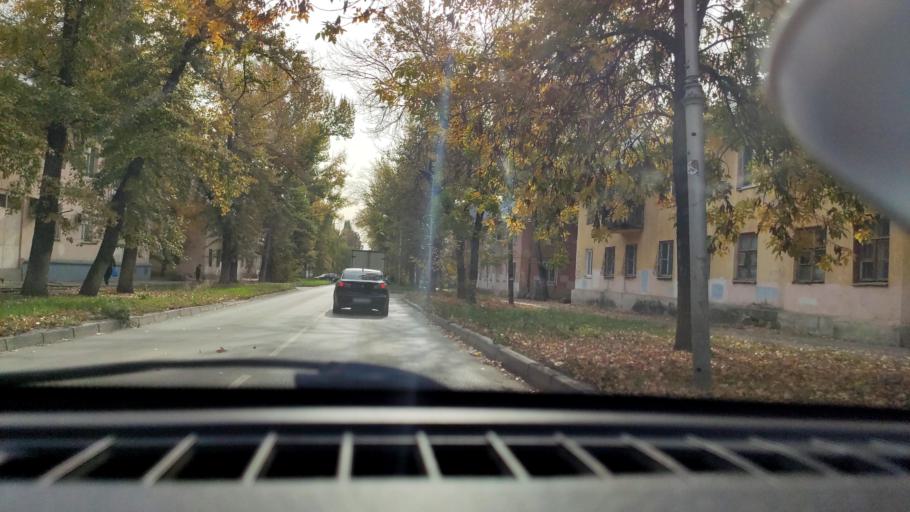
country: RU
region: Samara
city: Samara
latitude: 53.2278
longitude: 50.2655
